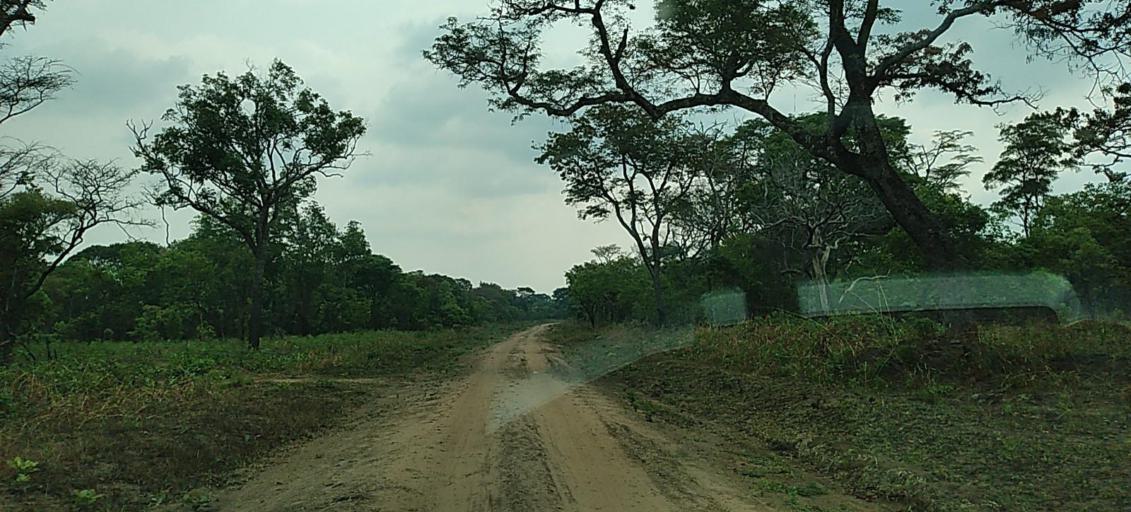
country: ZM
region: North-Western
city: Mwinilunga
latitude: -11.4135
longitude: 24.6127
